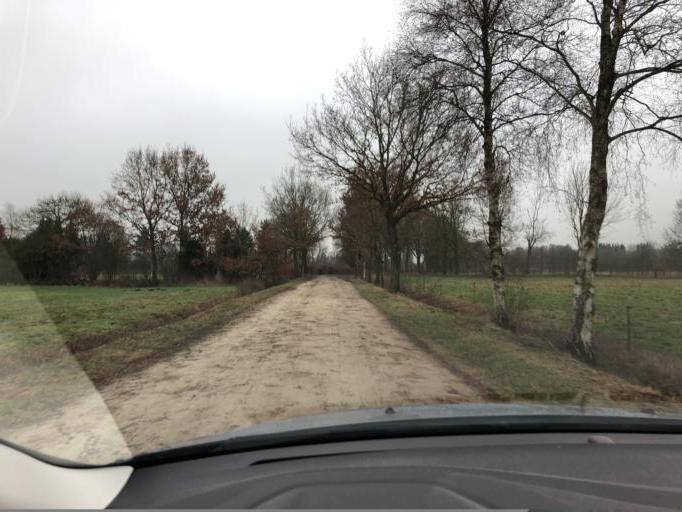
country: DE
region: Lower Saxony
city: Bad Zwischenahn
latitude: 53.1698
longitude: 8.0450
